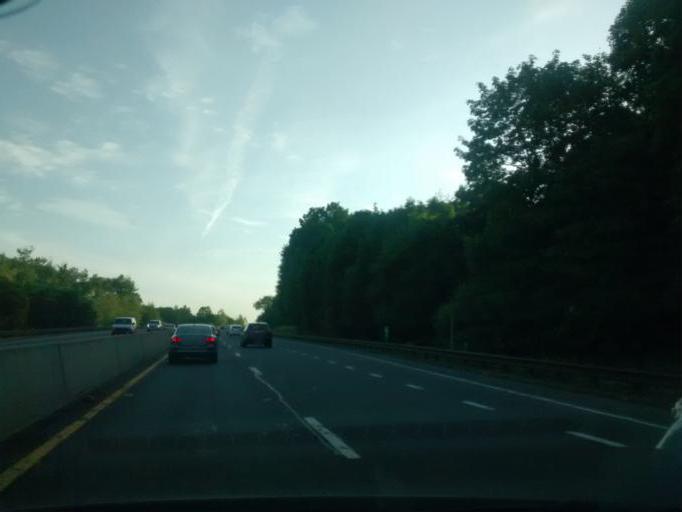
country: US
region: New York
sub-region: Westchester County
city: Purchase
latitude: 41.0238
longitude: -73.7060
